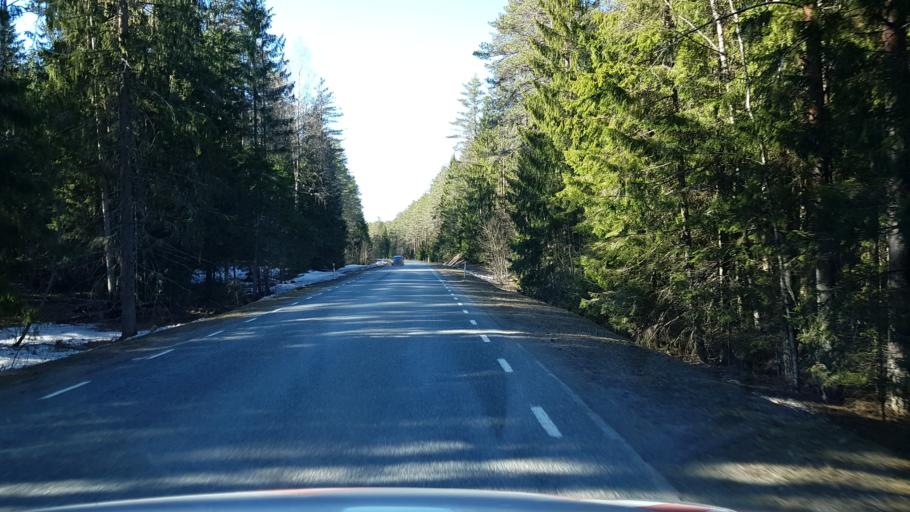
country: EE
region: Laeaene-Virumaa
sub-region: Vinni vald
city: Vinni
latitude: 59.2591
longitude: 26.6837
